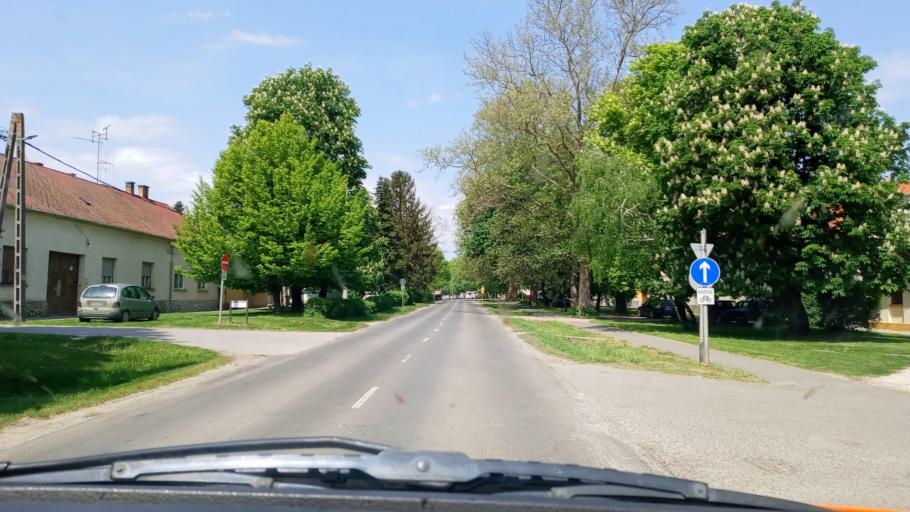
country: HU
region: Baranya
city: Boly
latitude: 45.9649
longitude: 18.5212
